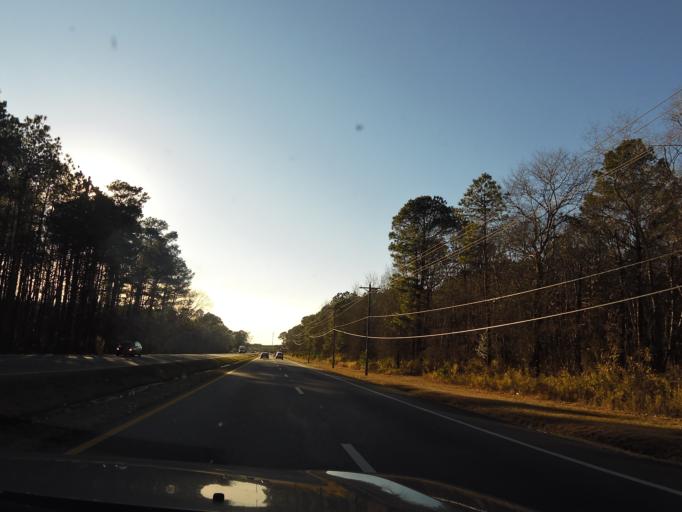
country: US
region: Virginia
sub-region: City of Suffolk
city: South Suffolk
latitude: 36.7024
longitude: -76.6967
